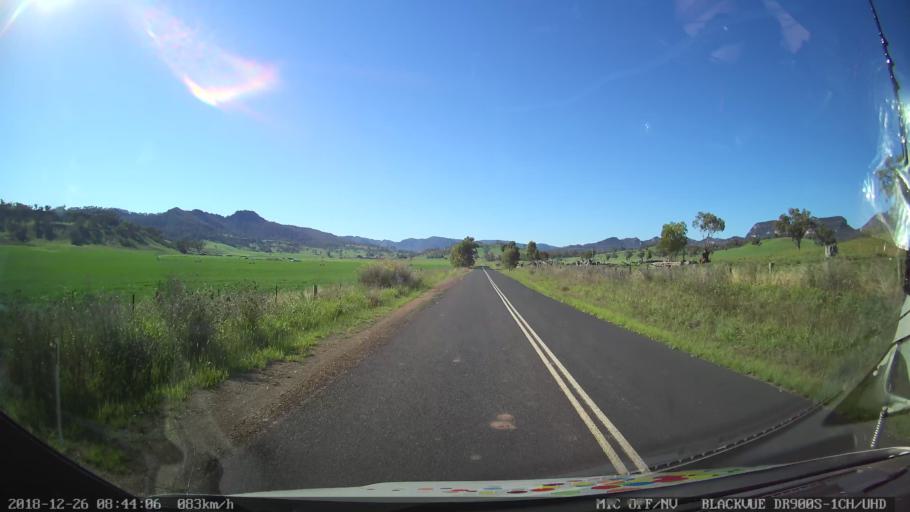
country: AU
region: New South Wales
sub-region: Mid-Western Regional
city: Kandos
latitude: -32.5107
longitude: 150.0800
